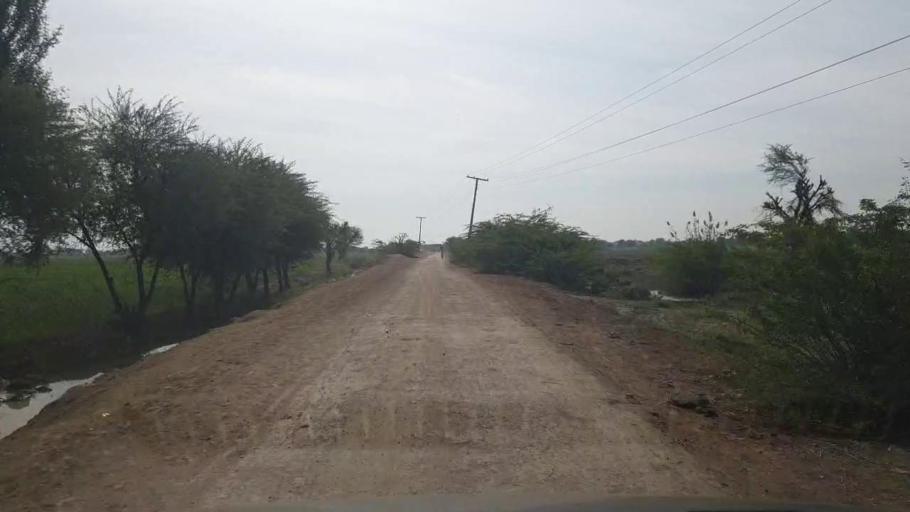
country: PK
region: Sindh
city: Umarkot
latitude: 25.3597
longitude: 69.6272
